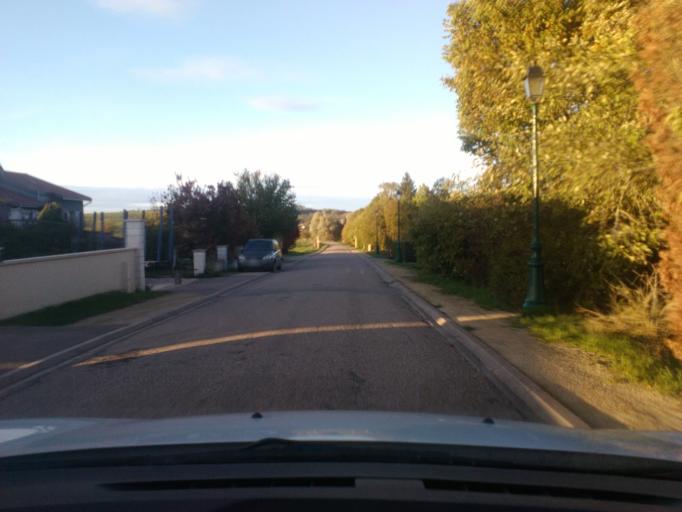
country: FR
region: Lorraine
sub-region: Departement des Vosges
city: Charmes
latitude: 48.3506
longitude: 6.2551
